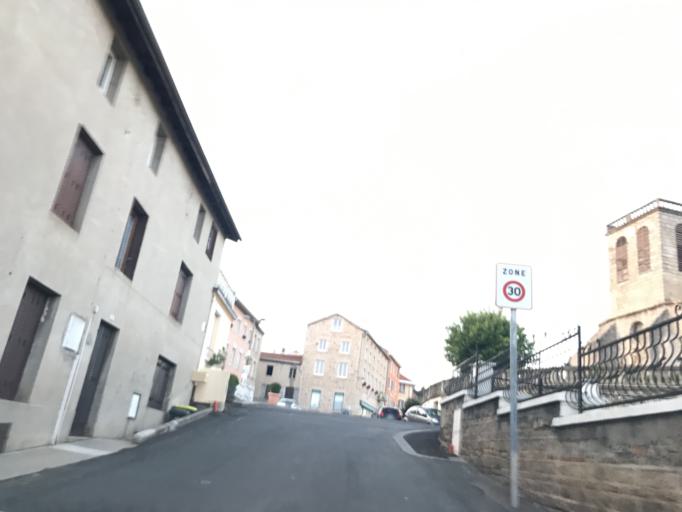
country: FR
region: Auvergne
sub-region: Departement du Puy-de-Dome
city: Saint-Remy-sur-Durolle
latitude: 45.8871
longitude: 3.5913
